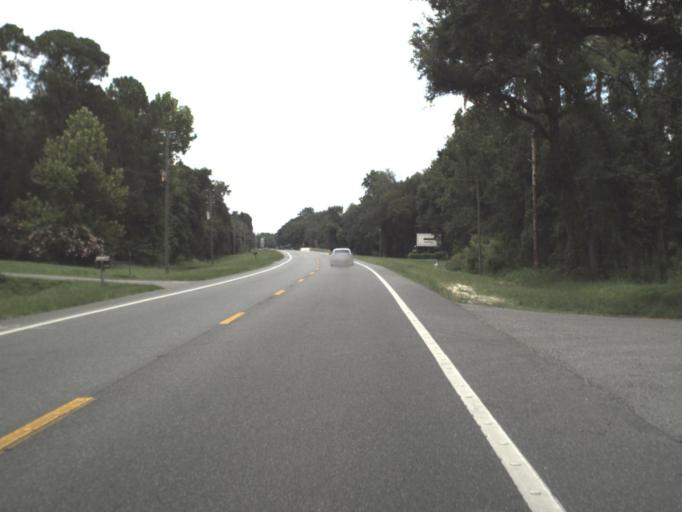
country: US
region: Florida
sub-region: Pasco County
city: Lacoochee
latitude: 28.4728
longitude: -82.1953
